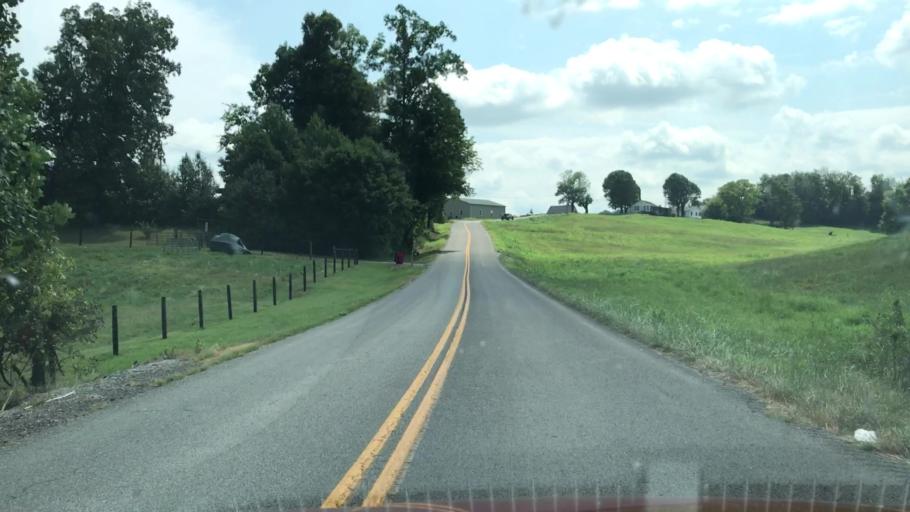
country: US
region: Kentucky
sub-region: Monroe County
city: Tompkinsville
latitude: 36.7167
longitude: -85.7127
